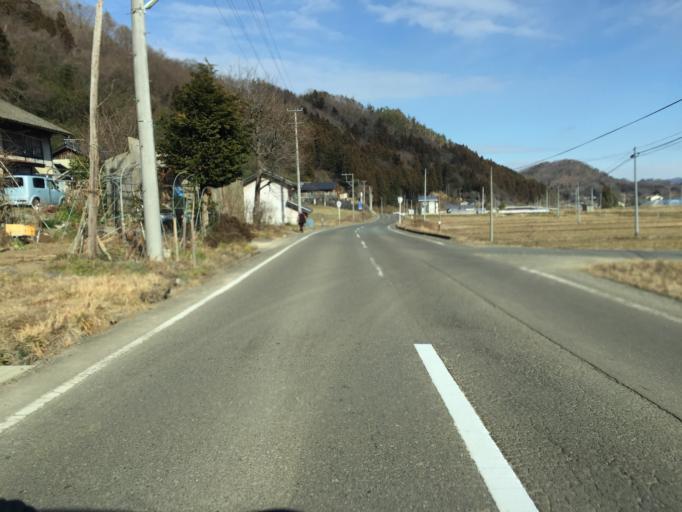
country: JP
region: Fukushima
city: Hobaramachi
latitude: 37.7557
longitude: 140.5690
